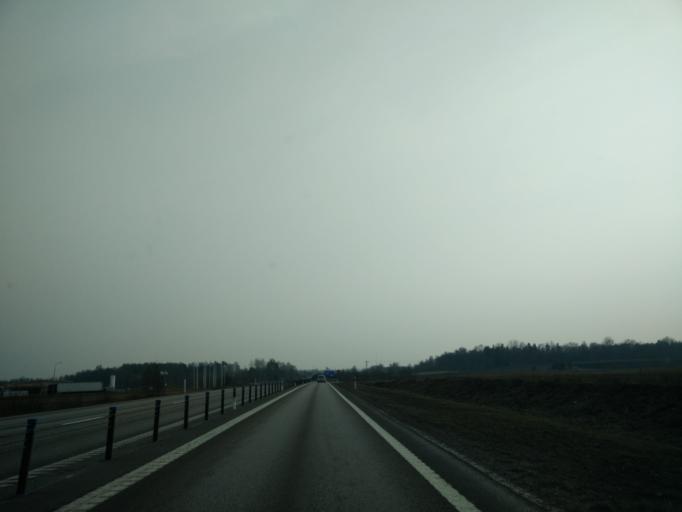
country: SE
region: Vaermland
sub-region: Karlstads Kommun
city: Karlstad
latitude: 59.4328
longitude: 13.4125
